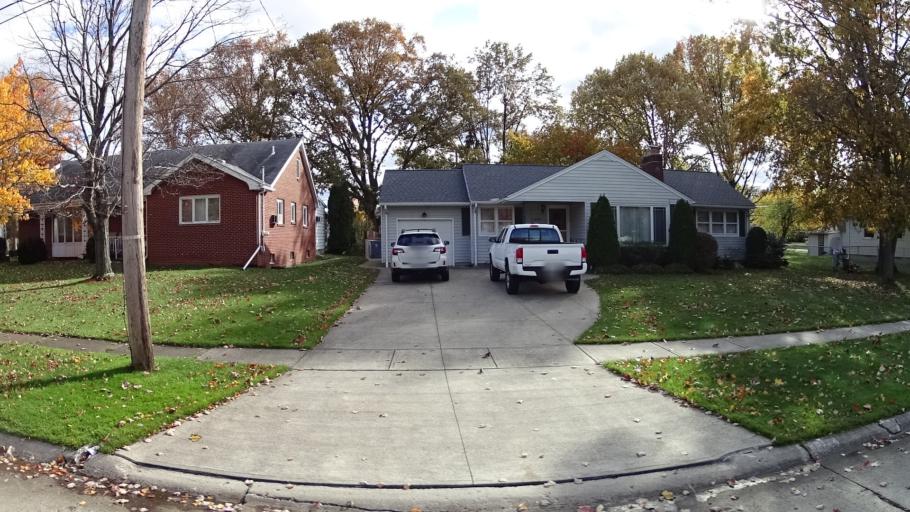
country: US
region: Ohio
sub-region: Lorain County
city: Lorain
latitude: 41.4237
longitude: -82.1892
